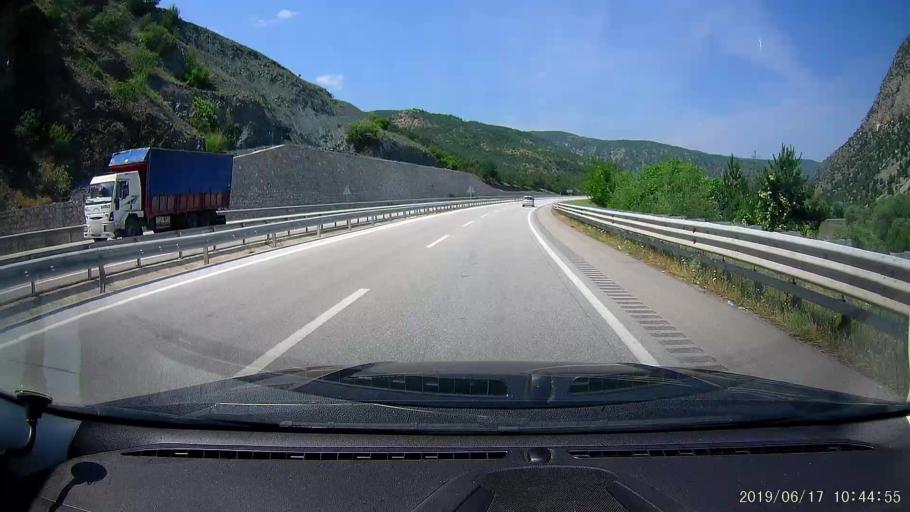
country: TR
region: Corum
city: Hacihamza
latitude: 41.0661
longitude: 34.5021
